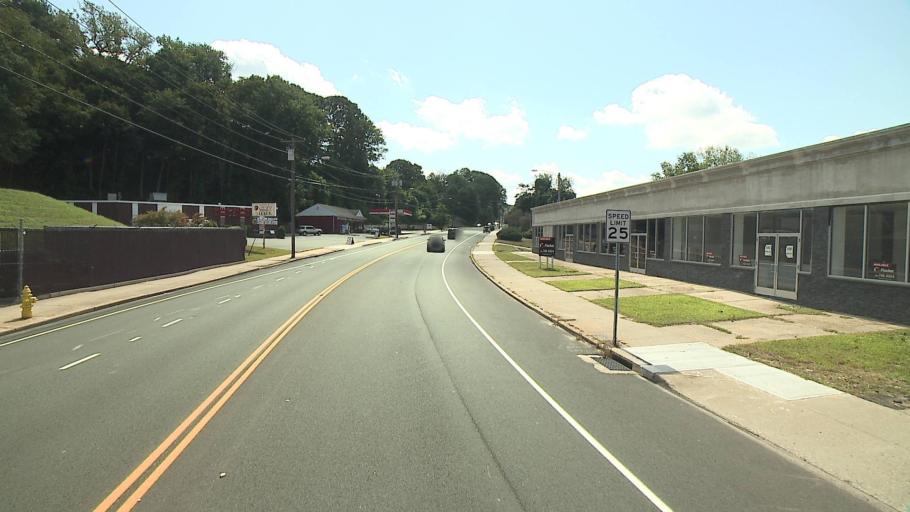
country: US
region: Connecticut
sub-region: New Haven County
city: Ansonia
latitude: 41.3362
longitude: -73.0761
